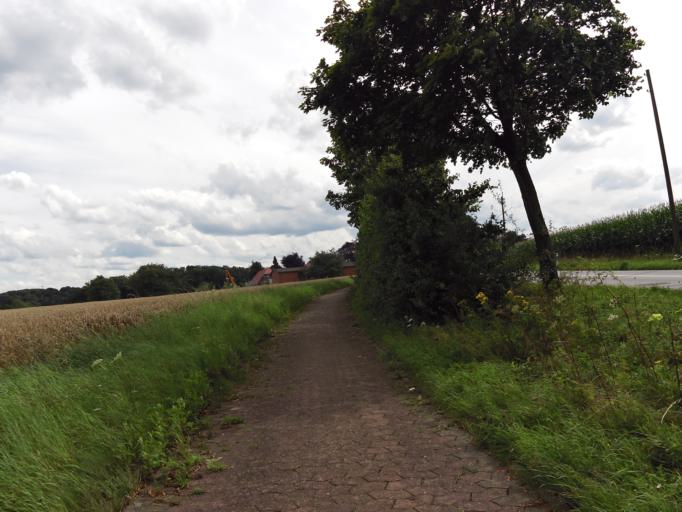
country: DE
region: North Rhine-Westphalia
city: Spenge
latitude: 52.1170
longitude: 8.4563
